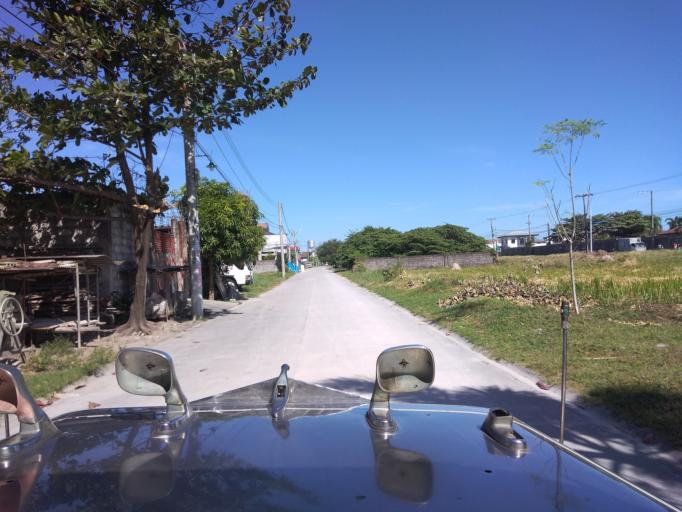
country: PH
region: Central Luzon
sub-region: Province of Pampanga
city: Calibutbut
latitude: 15.1063
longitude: 120.6062
